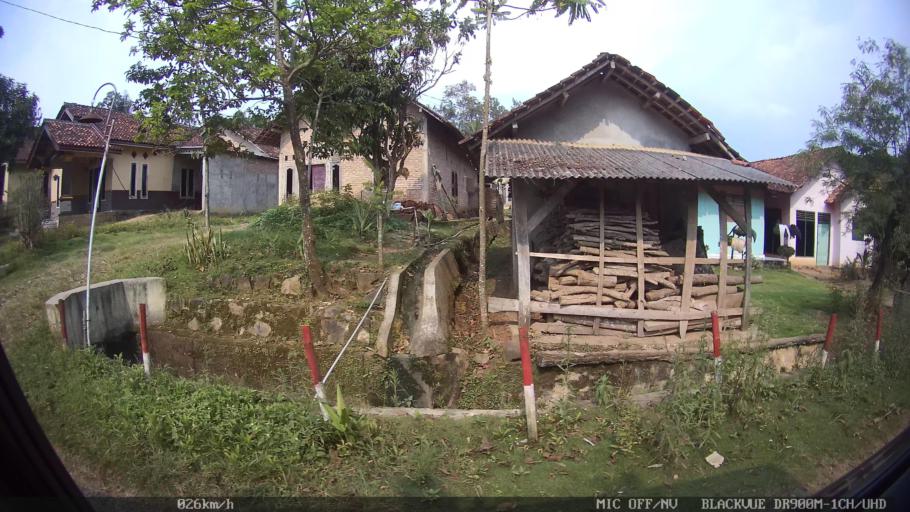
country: ID
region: Lampung
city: Gadingrejo
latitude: -5.4044
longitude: 105.0233
